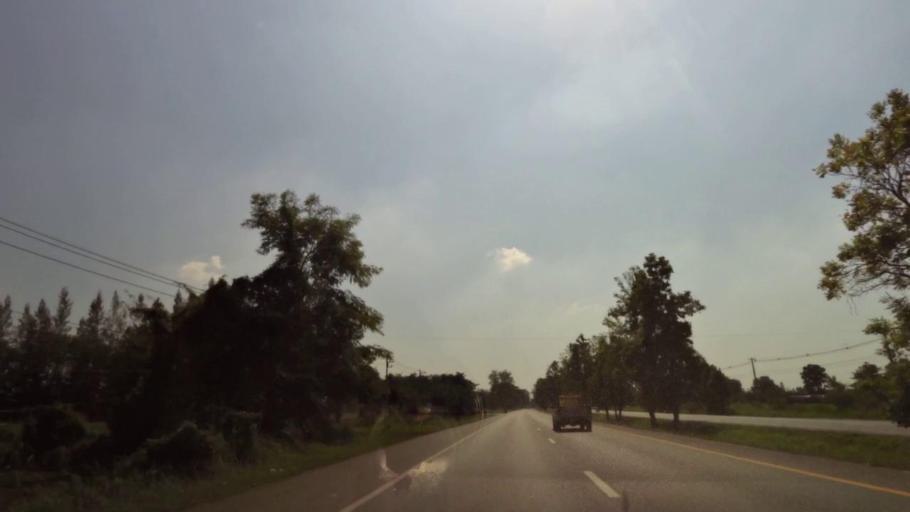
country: TH
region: Phichit
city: Bueng Na Rang
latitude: 16.1844
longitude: 100.1287
